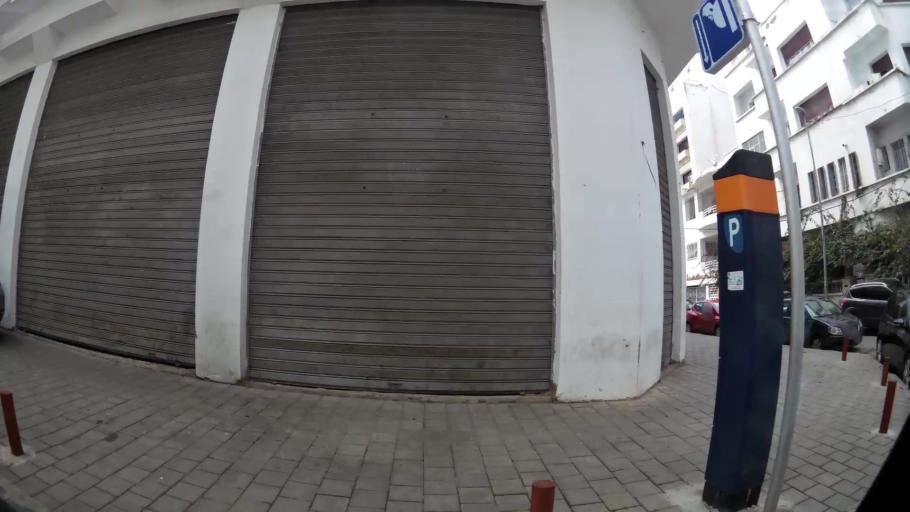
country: MA
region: Grand Casablanca
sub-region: Casablanca
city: Casablanca
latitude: 33.5929
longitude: -7.6303
